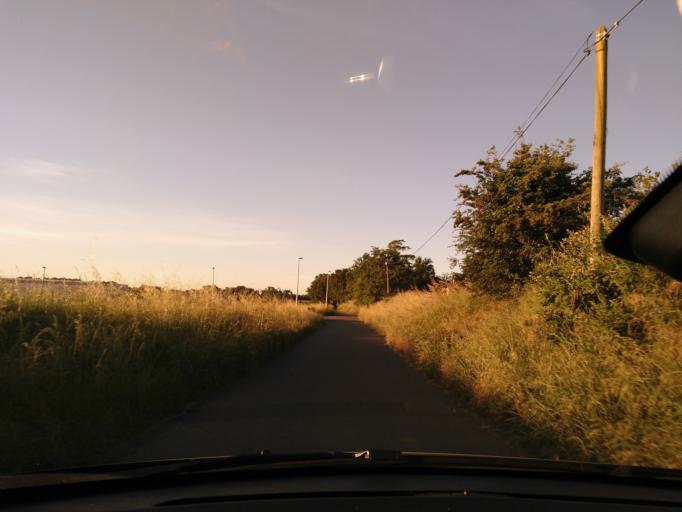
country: FR
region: Midi-Pyrenees
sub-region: Departement de la Haute-Garonne
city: Grenade
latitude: 43.7556
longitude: 1.2991
